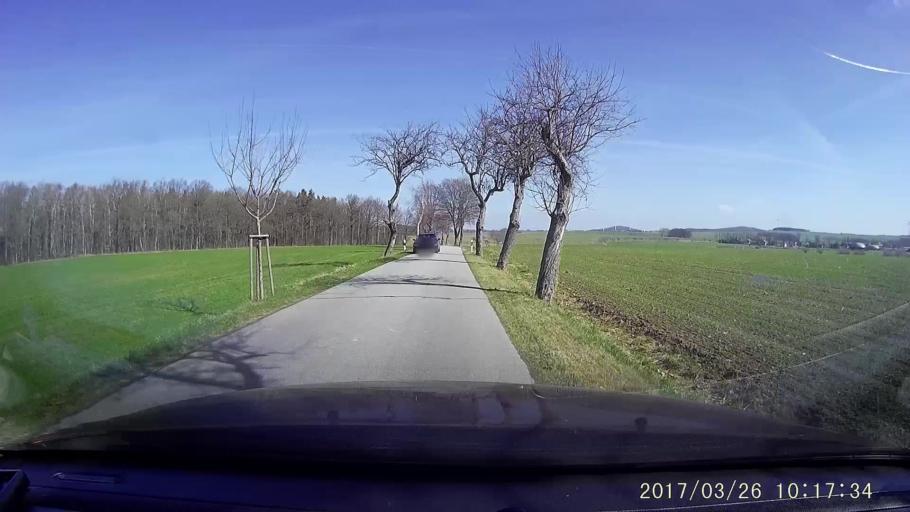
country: DE
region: Saxony
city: Herrnhut
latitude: 51.0655
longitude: 14.7623
